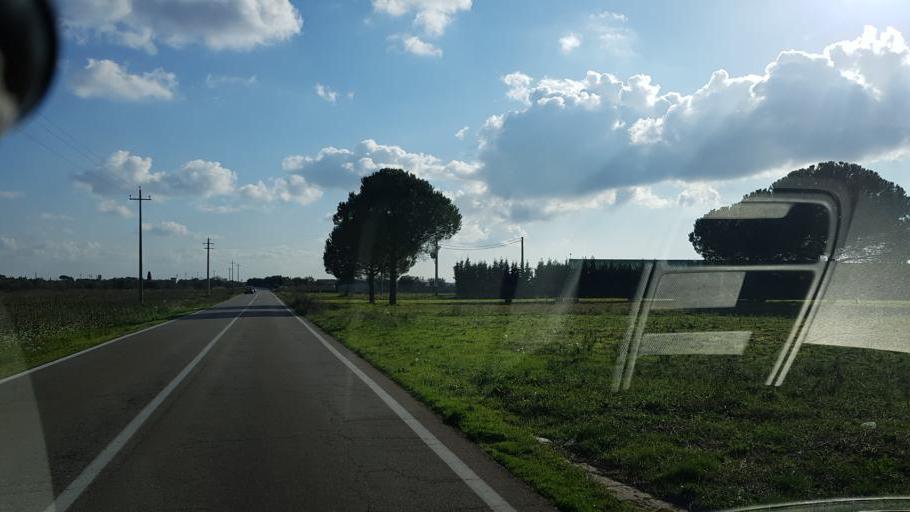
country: IT
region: Apulia
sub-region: Provincia di Lecce
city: Veglie
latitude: 40.3145
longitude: 17.9826
